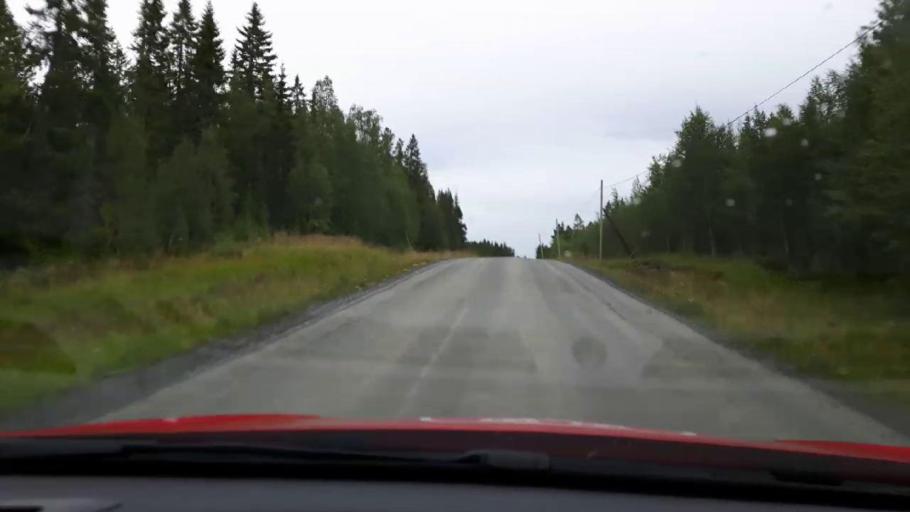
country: SE
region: Jaemtland
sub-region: Are Kommun
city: Jarpen
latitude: 63.4232
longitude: 13.3447
